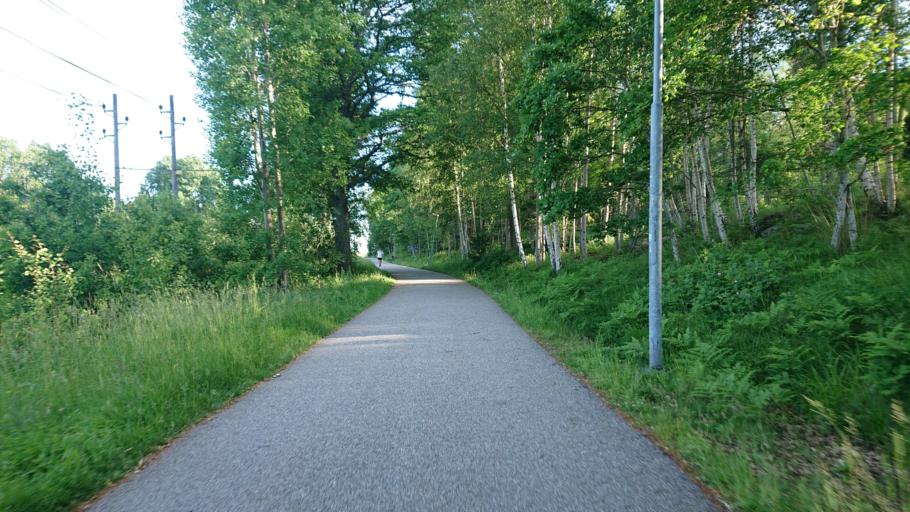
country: SE
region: Stockholm
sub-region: Osterakers Kommun
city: Akersberga
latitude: 59.4940
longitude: 18.3021
